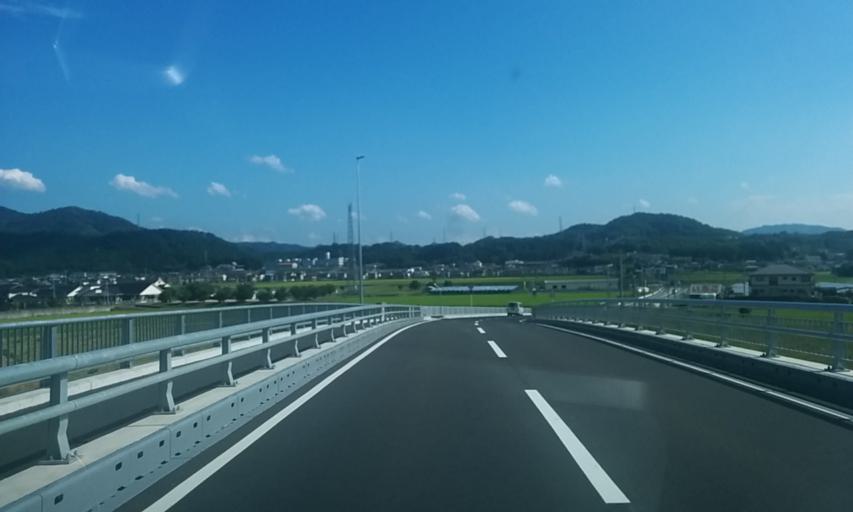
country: JP
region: Kyoto
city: Fukuchiyama
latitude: 35.3084
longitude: 135.1707
